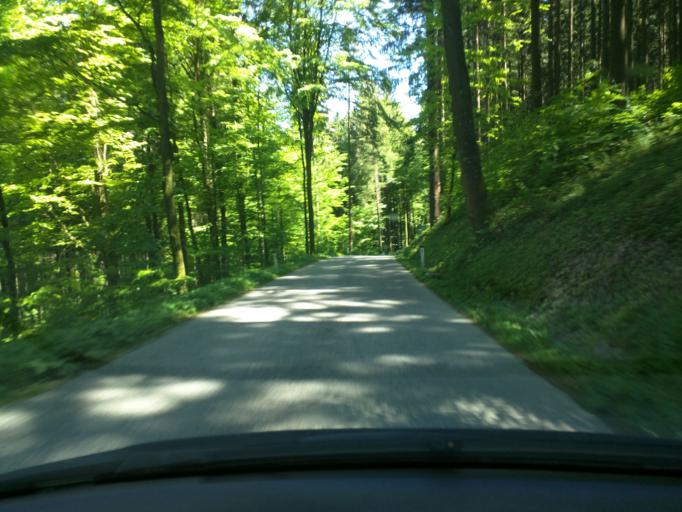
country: AT
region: Lower Austria
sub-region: Politischer Bezirk Melk
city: Blindenmarkt
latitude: 48.1585
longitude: 14.9745
